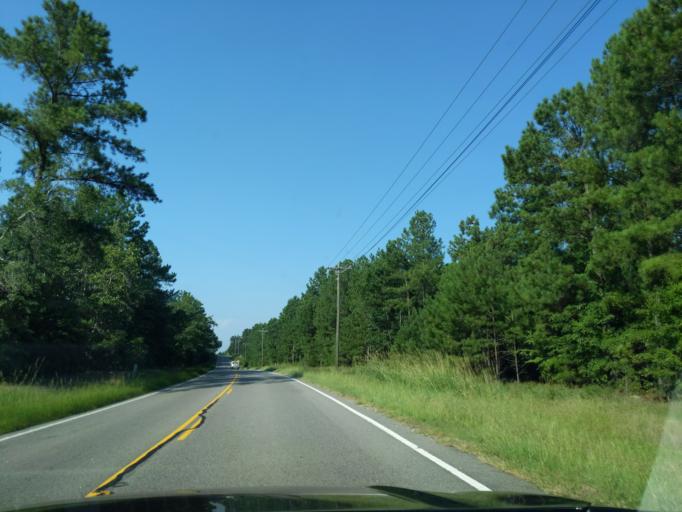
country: US
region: South Carolina
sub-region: Newberry County
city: Prosperity
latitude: 34.1205
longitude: -81.5541
